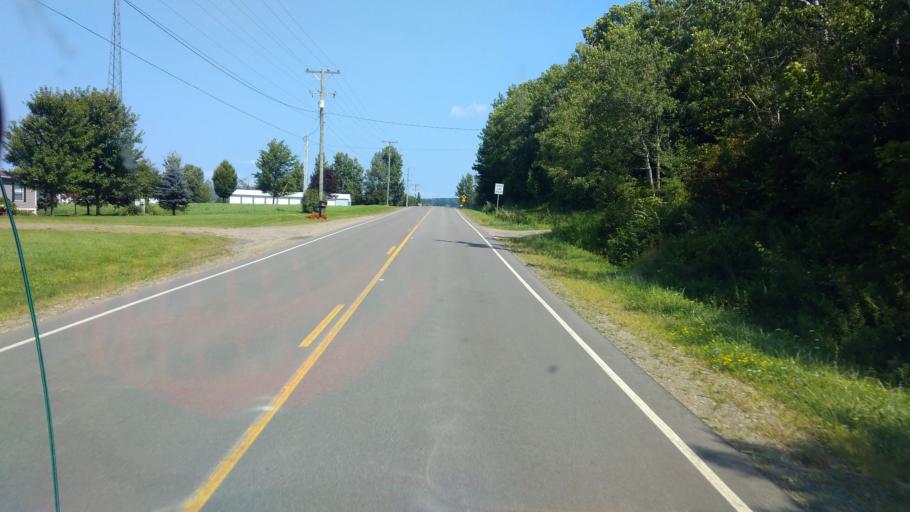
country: US
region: New York
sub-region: Allegany County
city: Belmont
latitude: 42.2940
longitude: -78.0262
